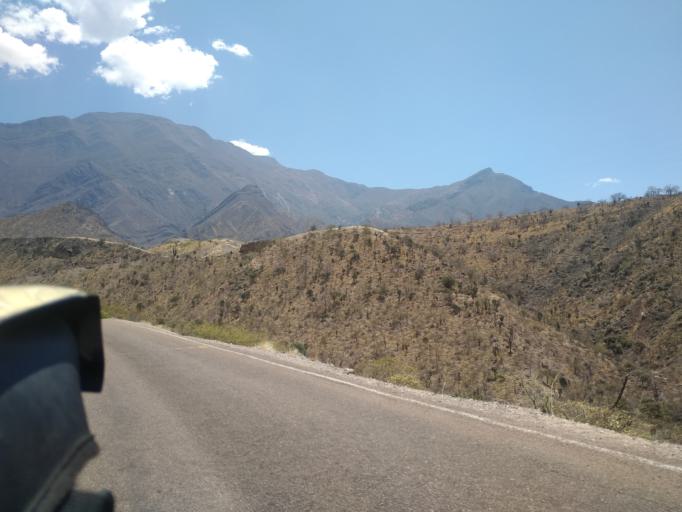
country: PE
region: Amazonas
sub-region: Provincia de Chachapoyas
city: Balsas
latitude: -6.8527
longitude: -78.0348
